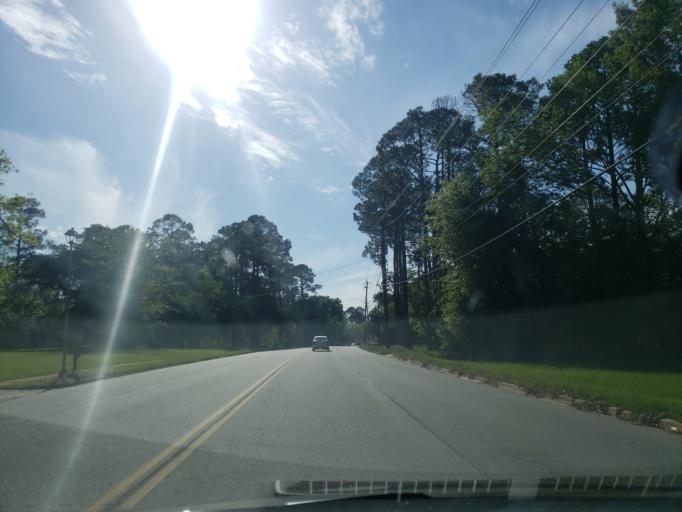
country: US
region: Georgia
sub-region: Dougherty County
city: Albany
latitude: 31.5902
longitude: -84.1807
